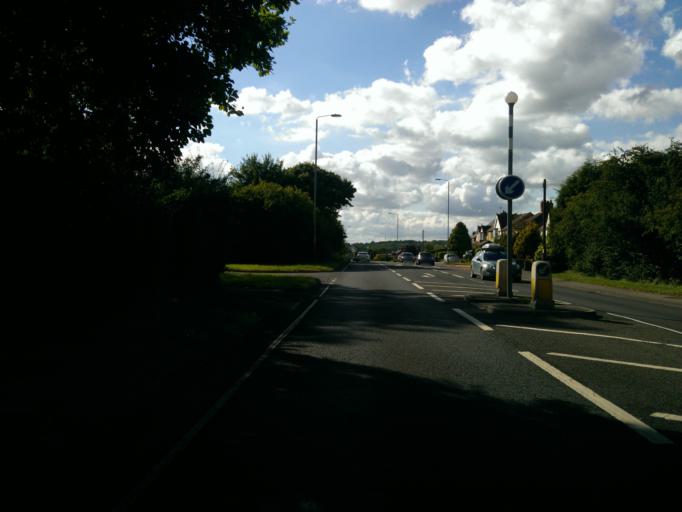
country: GB
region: England
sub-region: Warwickshire
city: Atherstone
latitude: 52.5891
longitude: -1.5859
